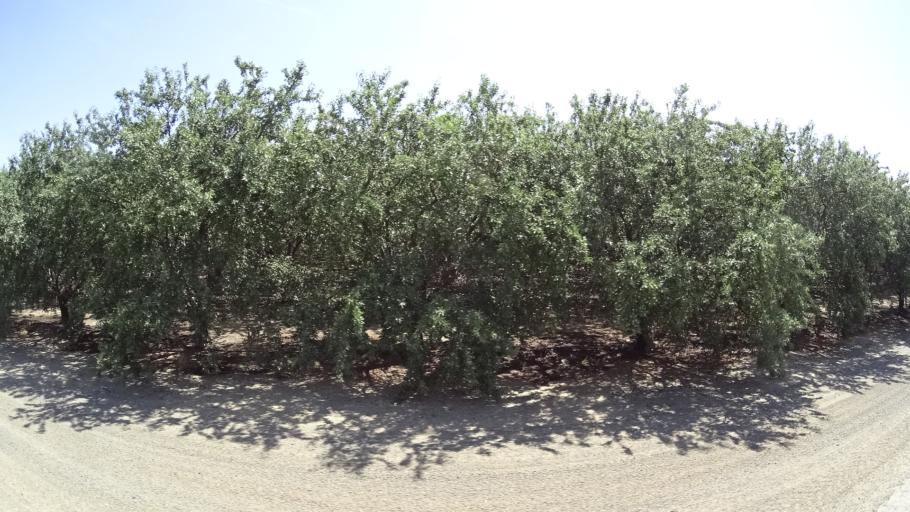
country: US
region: California
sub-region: Kings County
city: Kettleman City
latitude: 36.0976
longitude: -120.0037
